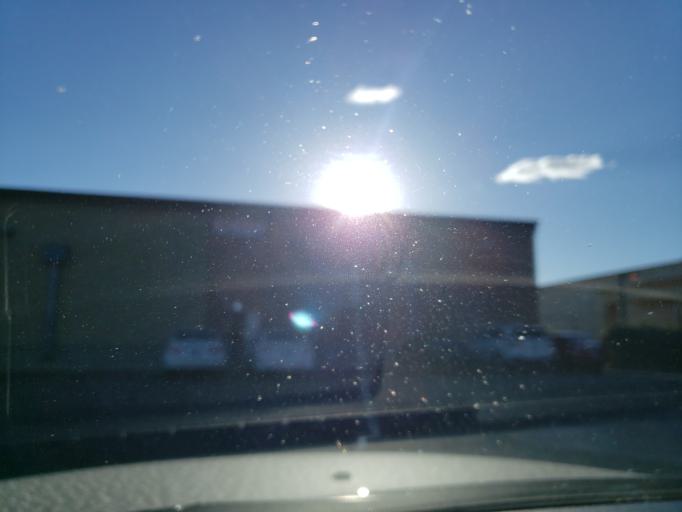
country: US
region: Arizona
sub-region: Maricopa County
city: Cave Creek
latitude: 33.7543
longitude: -111.9900
